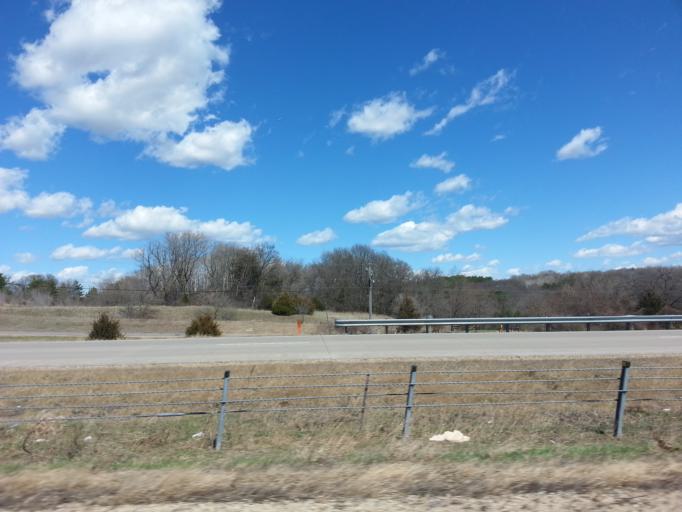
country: US
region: Minnesota
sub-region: Washington County
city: Cottage Grove
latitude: 44.8015
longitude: -92.9049
